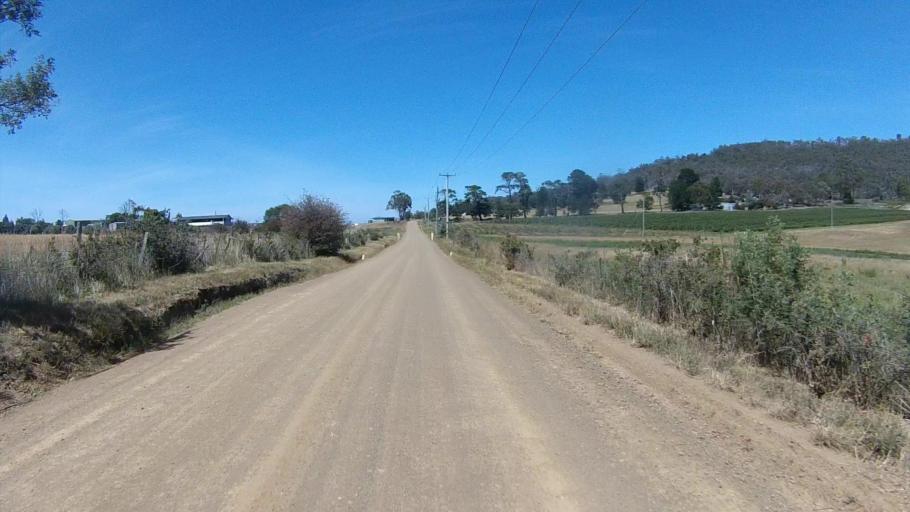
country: AU
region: Tasmania
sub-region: Sorell
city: Sorell
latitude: -42.7850
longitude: 147.6388
